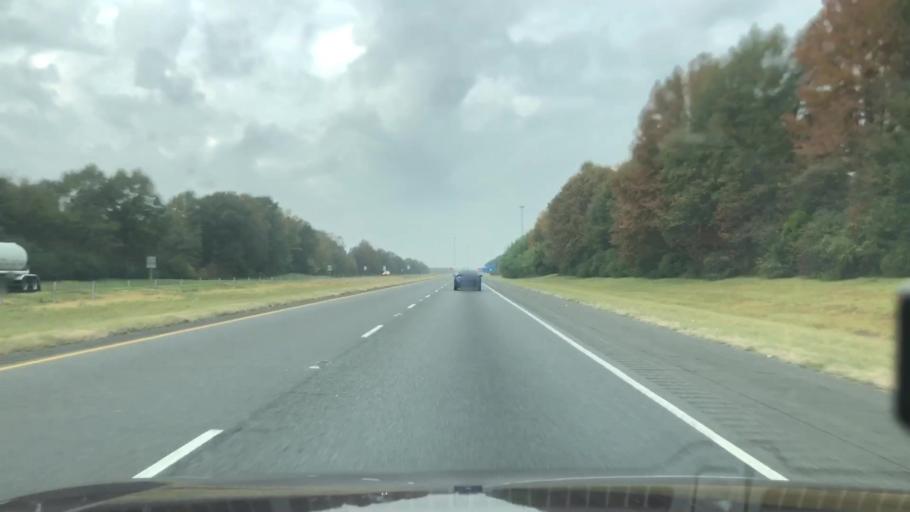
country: US
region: Louisiana
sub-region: Richland Parish
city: Delhi
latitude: 32.4406
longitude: -91.4791
